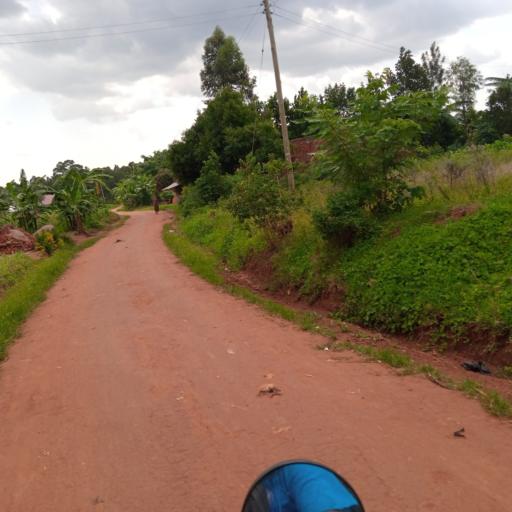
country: UG
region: Eastern Region
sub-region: Mbale District
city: Mbale
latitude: 1.1238
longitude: 34.1821
